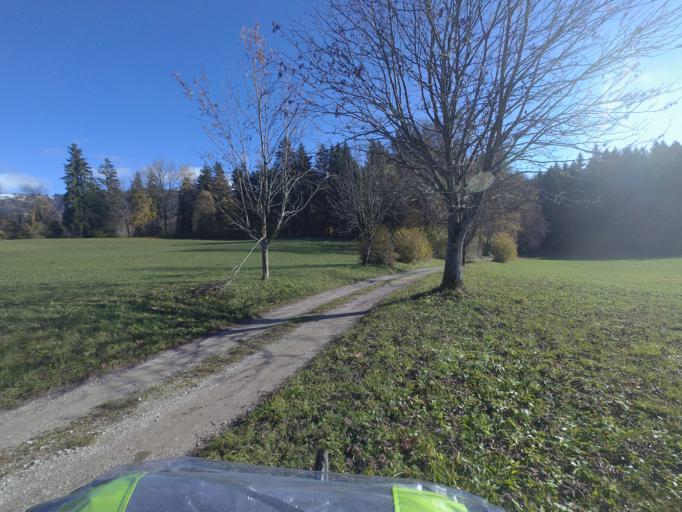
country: AT
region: Salzburg
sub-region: Politischer Bezirk Hallein
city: Adnet
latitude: 47.6713
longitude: 13.1474
